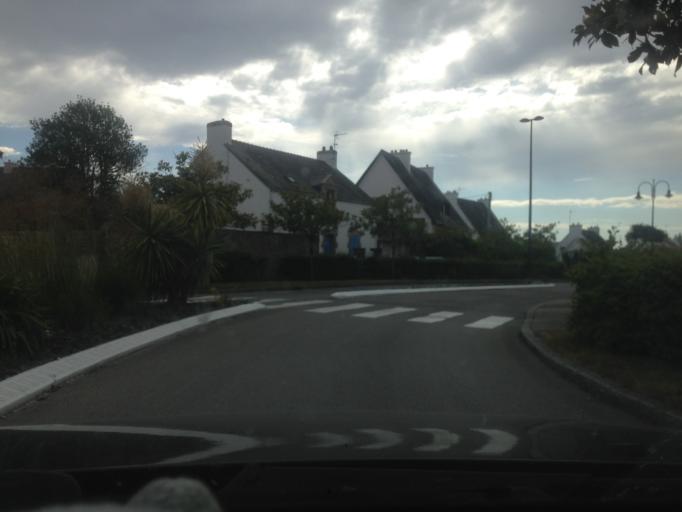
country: FR
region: Brittany
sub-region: Departement du Morbihan
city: Carnac
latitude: 47.5852
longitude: -3.0838
